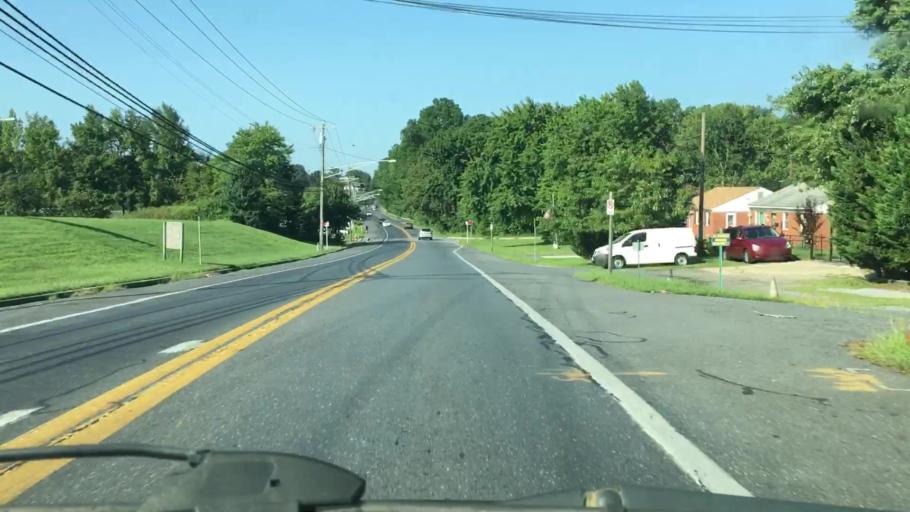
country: US
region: Maryland
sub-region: Prince George's County
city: Seabrook
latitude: 38.9785
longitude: -76.8354
